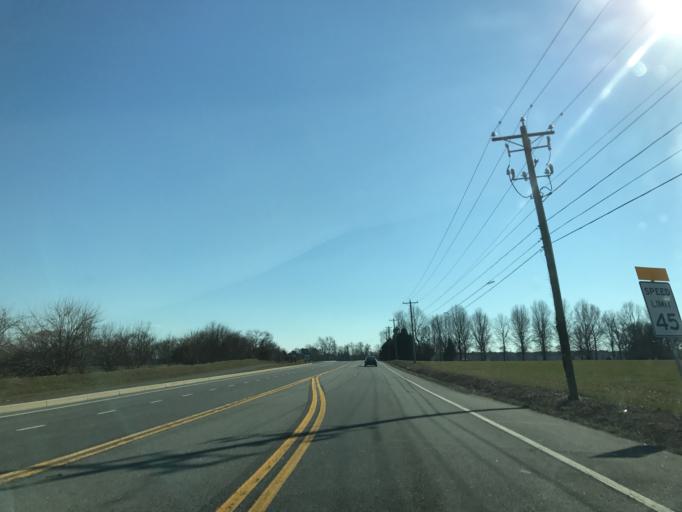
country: US
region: Maryland
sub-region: Queen Anne's County
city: Centreville
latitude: 39.0310
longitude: -76.0772
